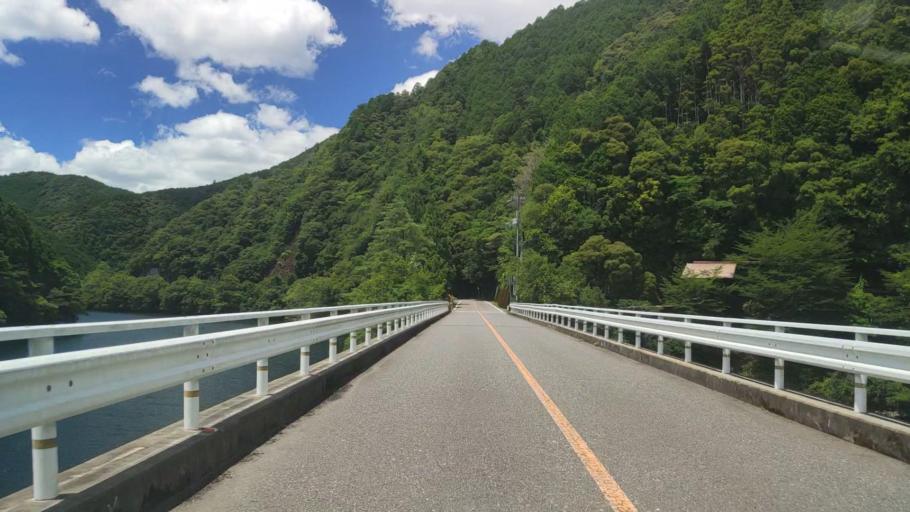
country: JP
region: Mie
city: Owase
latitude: 33.9974
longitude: 136.0229
